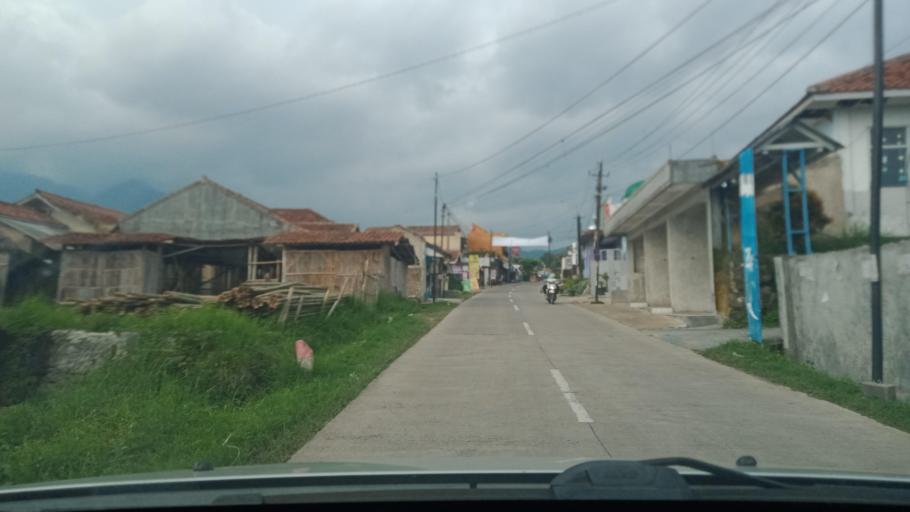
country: ID
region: West Java
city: Lembang
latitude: -6.8131
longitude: 107.5765
